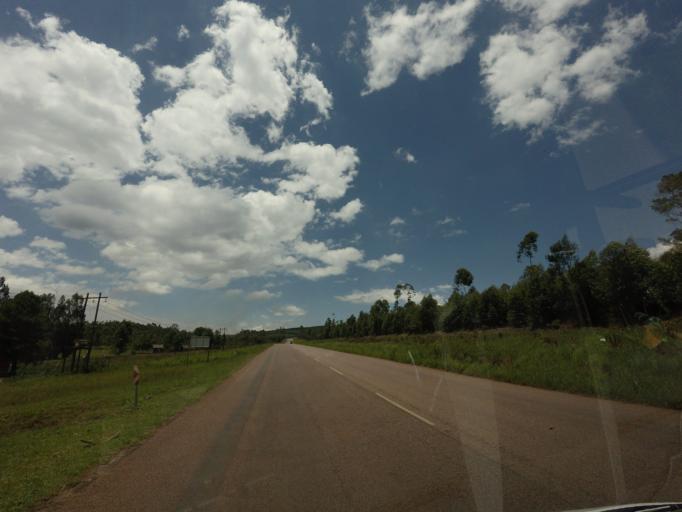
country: ZA
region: Mpumalanga
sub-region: Ehlanzeni District
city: Graksop
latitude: -25.0807
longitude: 30.7919
